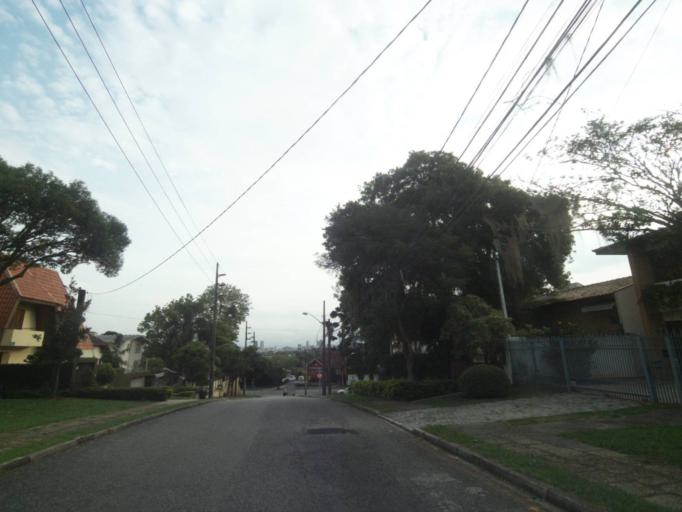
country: BR
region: Parana
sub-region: Curitiba
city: Curitiba
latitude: -25.4019
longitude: -49.2826
